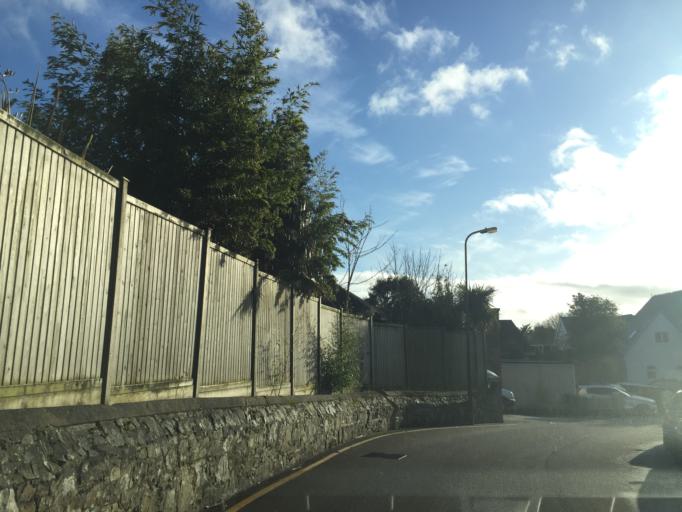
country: JE
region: St Helier
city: Saint Helier
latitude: 49.1981
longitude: -2.1338
